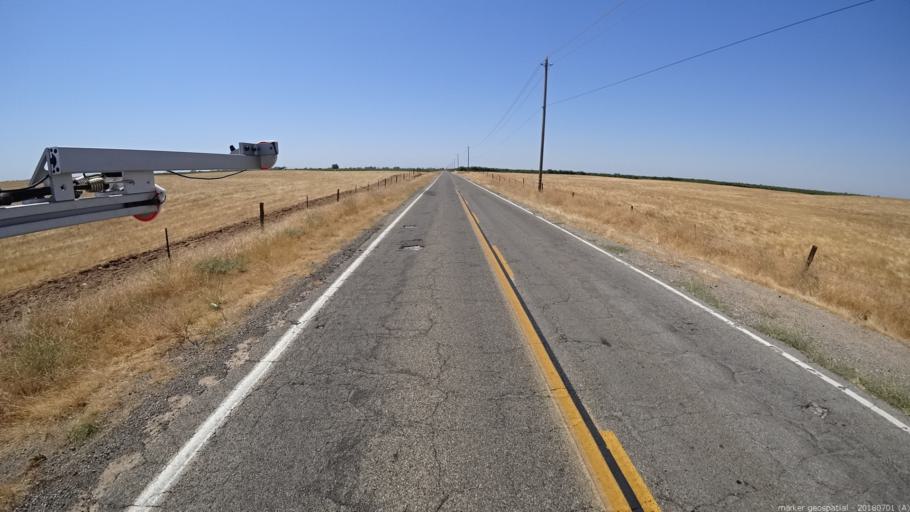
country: US
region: California
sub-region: Madera County
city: Madera Acres
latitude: 37.0140
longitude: -120.0289
